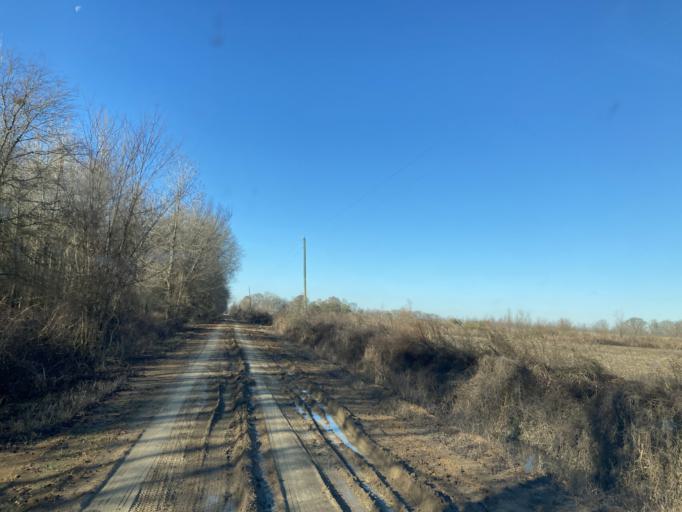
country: US
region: Mississippi
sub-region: Yazoo County
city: Yazoo City
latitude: 32.9371
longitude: -90.5607
